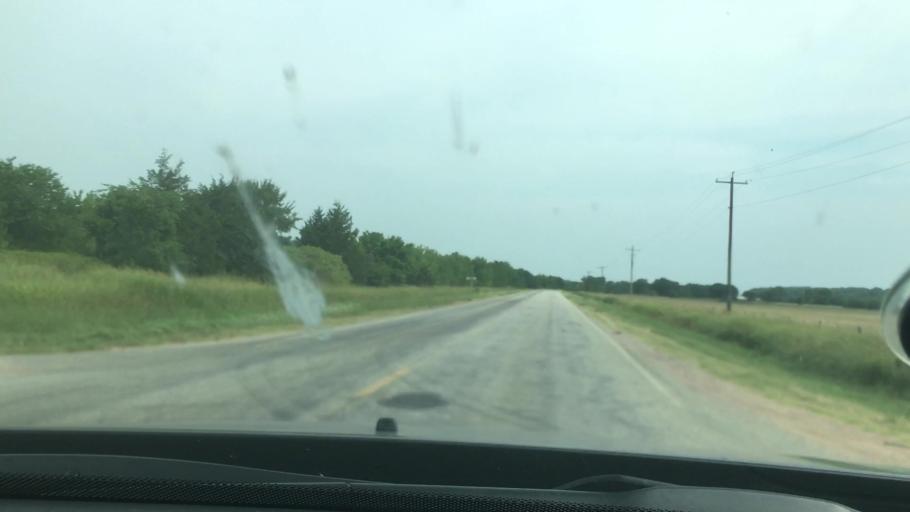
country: US
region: Oklahoma
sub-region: Johnston County
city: Tishomingo
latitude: 34.3458
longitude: -96.4230
